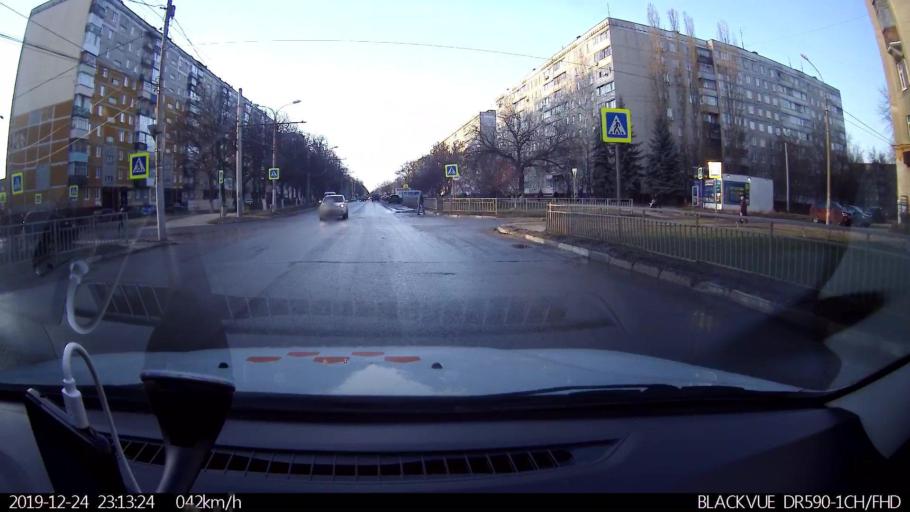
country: RU
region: Nizjnij Novgorod
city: Gorbatovka
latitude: 56.2522
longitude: 43.8630
